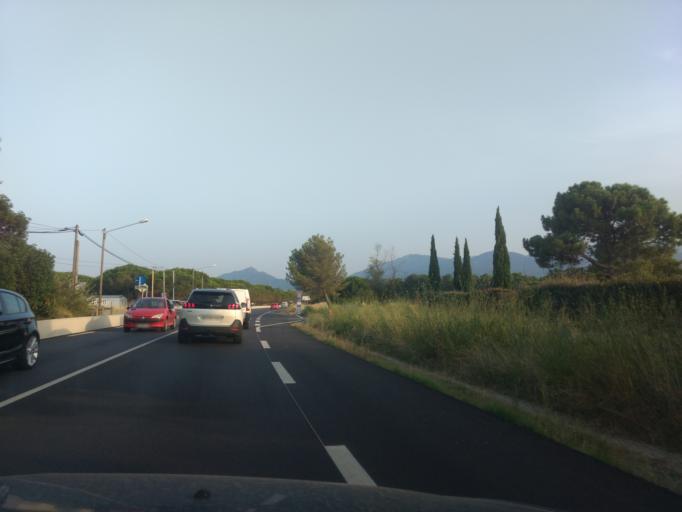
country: FR
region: Languedoc-Roussillon
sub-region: Departement des Pyrenees-Orientales
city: Argelers
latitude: 42.5707
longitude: 3.0406
